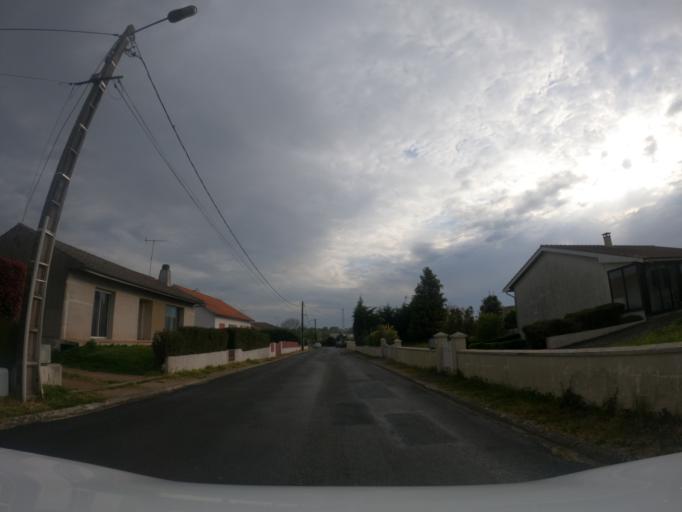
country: FR
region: Pays de la Loire
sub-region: Departement de la Vendee
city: Le Champ-Saint-Pere
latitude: 46.5093
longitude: -1.3501
